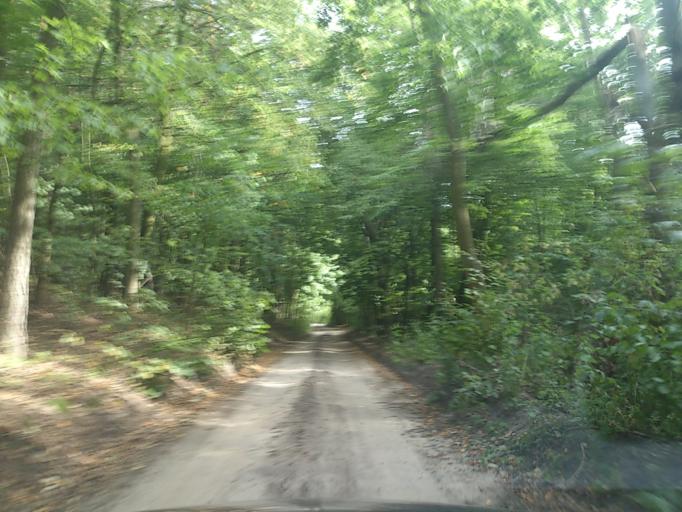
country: PL
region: Kujawsko-Pomorskie
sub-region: Powiat golubsko-dobrzynski
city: Golub-Dobrzyn
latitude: 53.1237
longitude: 19.0632
